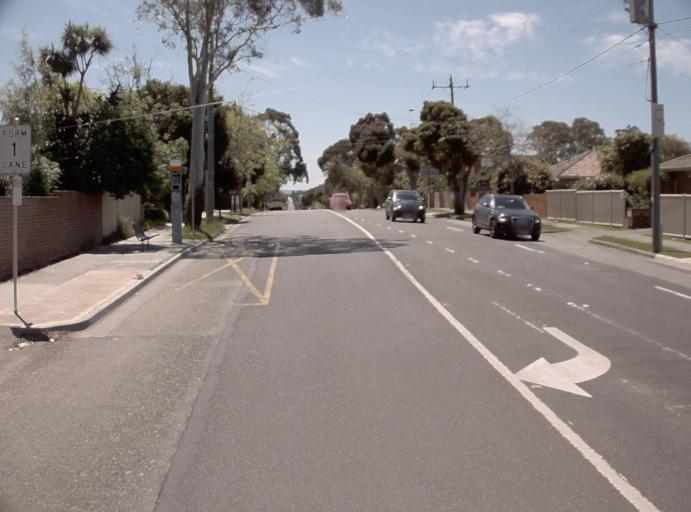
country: AU
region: Victoria
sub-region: Whitehorse
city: Blackburn North
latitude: -37.8108
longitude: 145.1577
